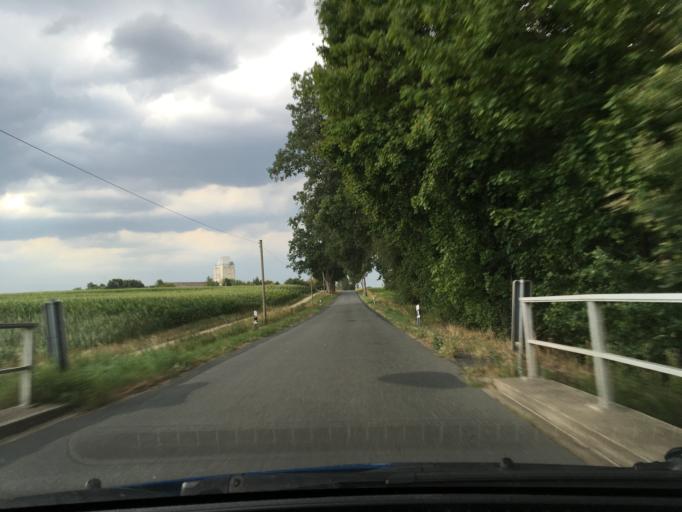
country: DE
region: Lower Saxony
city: Hanstedt Eins
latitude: 53.0540
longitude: 10.3803
